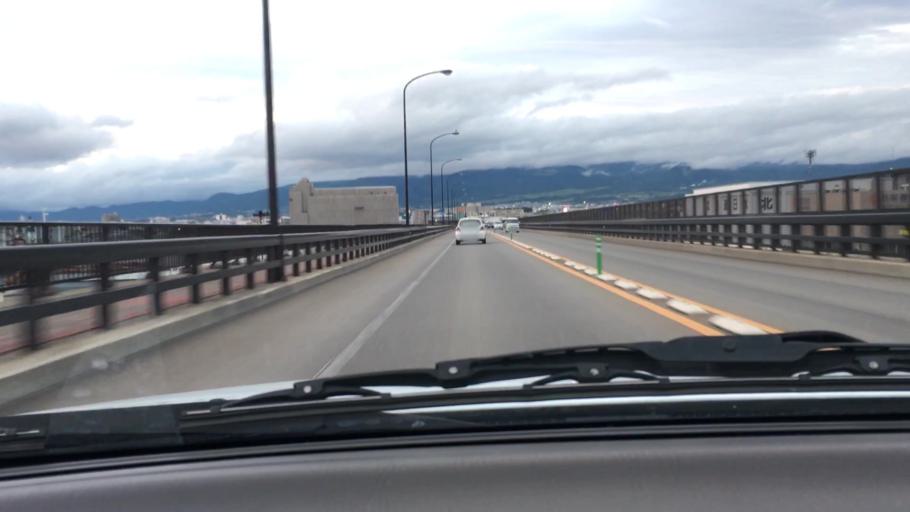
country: JP
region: Hokkaido
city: Hakodate
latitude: 41.7816
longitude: 140.7267
